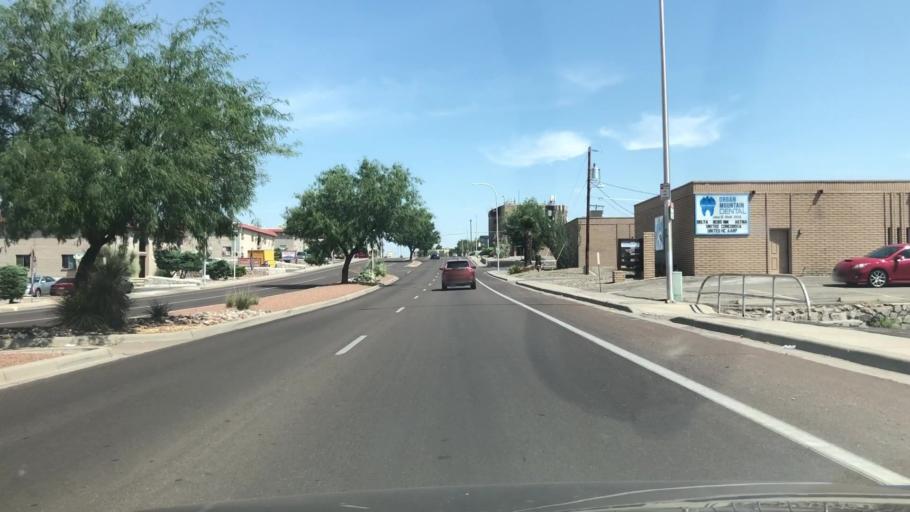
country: US
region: New Mexico
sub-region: Dona Ana County
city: University Park
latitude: 32.3033
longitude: -106.7376
